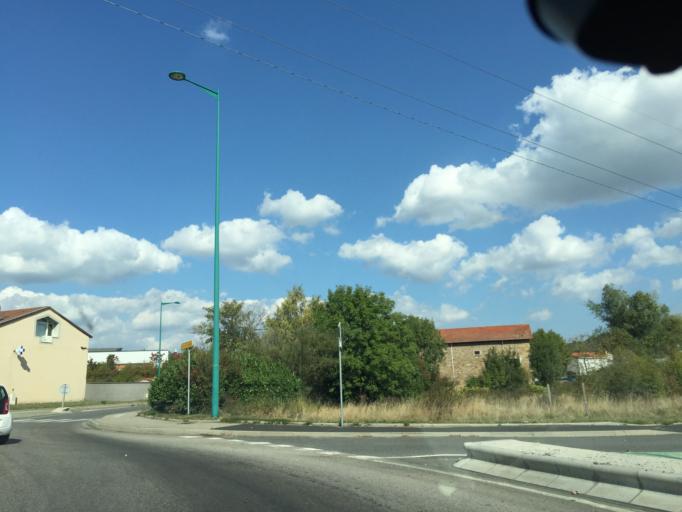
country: FR
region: Rhone-Alpes
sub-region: Departement de la Loire
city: La Talaudiere
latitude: 45.4616
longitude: 4.4173
